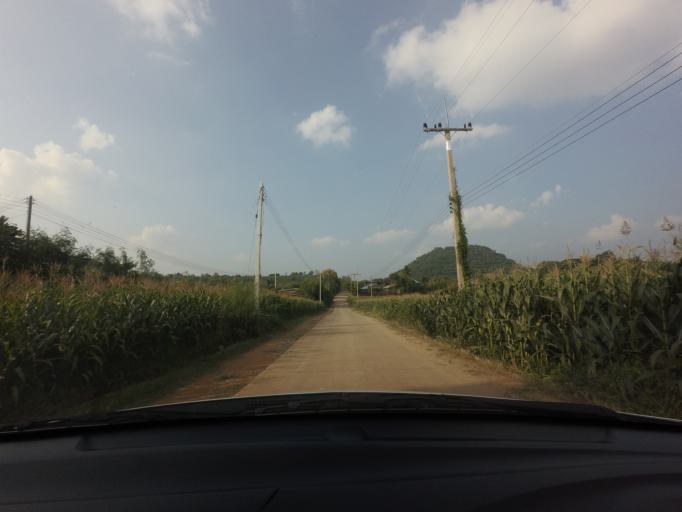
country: TH
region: Nakhon Ratchasima
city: Pak Chong
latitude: 14.5248
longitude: 101.5744
